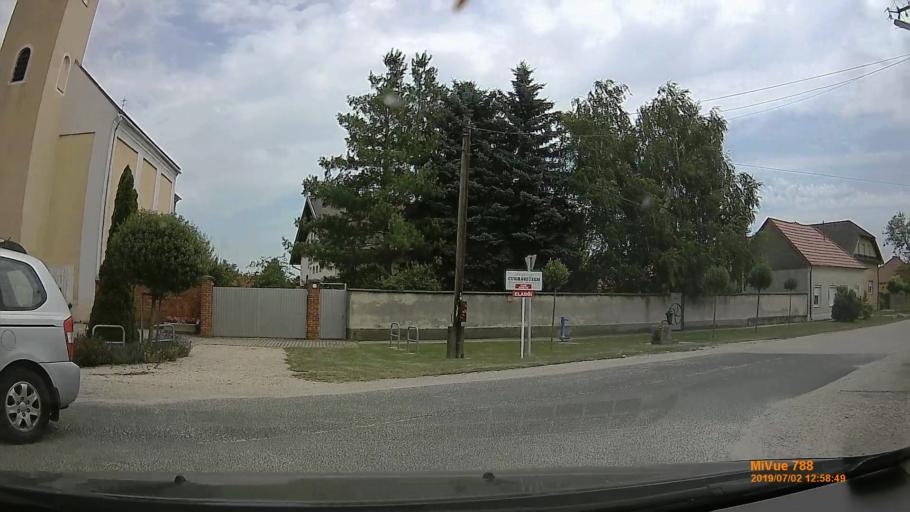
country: HU
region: Gyor-Moson-Sopron
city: Halaszi
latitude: 47.8590
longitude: 17.3216
